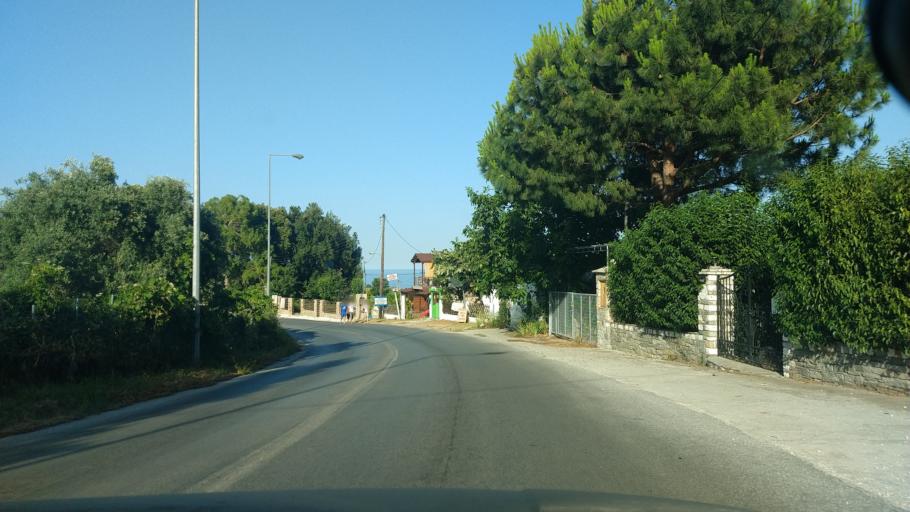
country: GR
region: East Macedonia and Thrace
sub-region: Nomos Kavalas
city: Potamia
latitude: 40.7142
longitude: 24.7367
